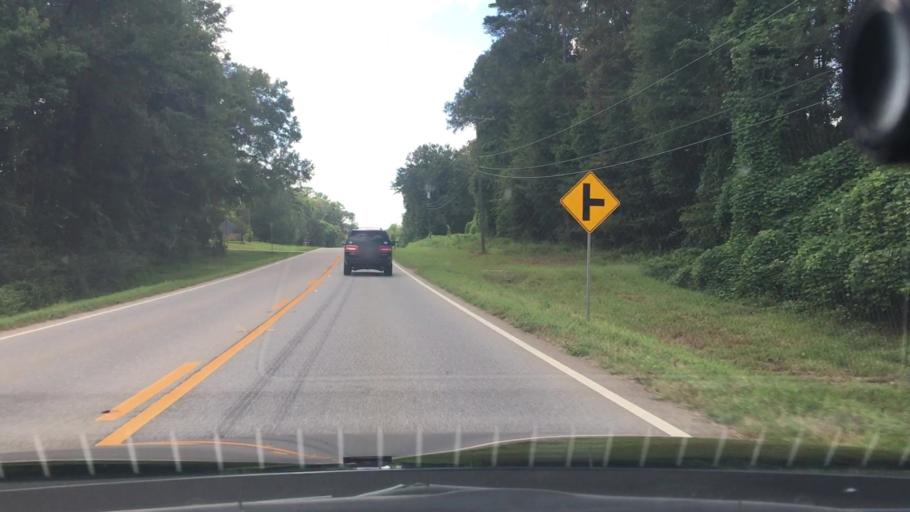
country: US
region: Georgia
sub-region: Putnam County
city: Eatonton
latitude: 33.3175
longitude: -83.4230
